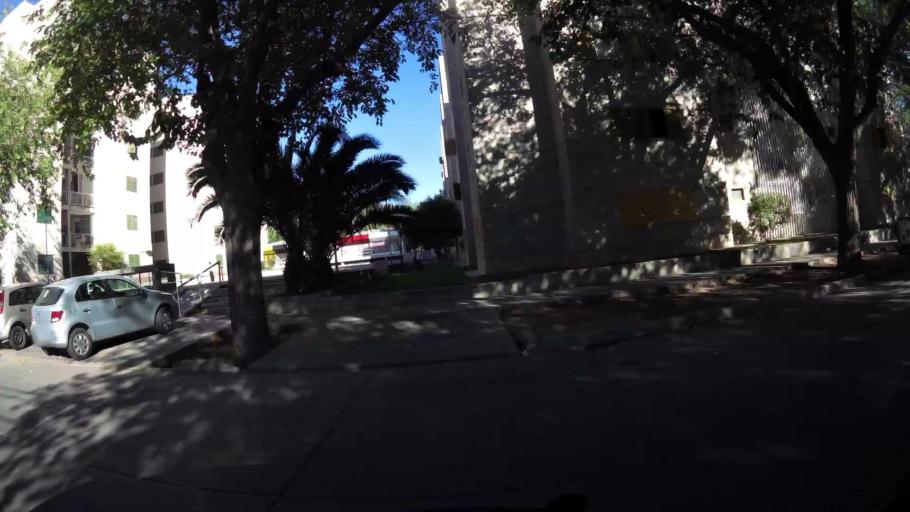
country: AR
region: Mendoza
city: Las Heras
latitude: -32.8692
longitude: -68.8365
